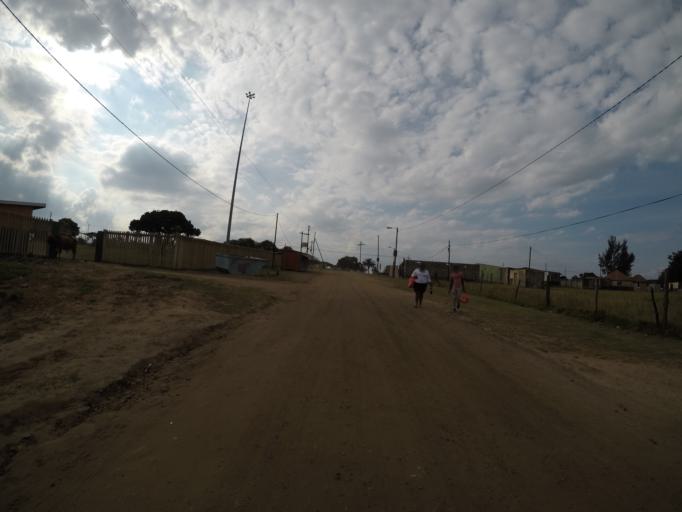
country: ZA
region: KwaZulu-Natal
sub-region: uThungulu District Municipality
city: Richards Bay
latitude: -28.7391
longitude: 32.1045
